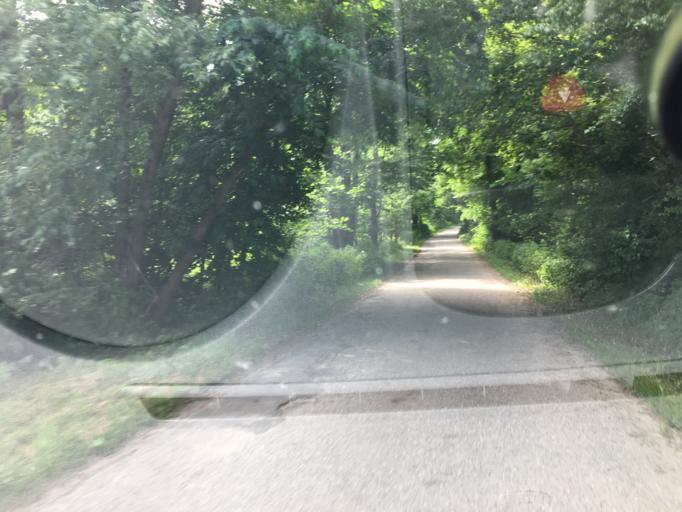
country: DK
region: South Denmark
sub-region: Sonderborg Kommune
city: Dybbol
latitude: 54.9450
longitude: 9.7491
